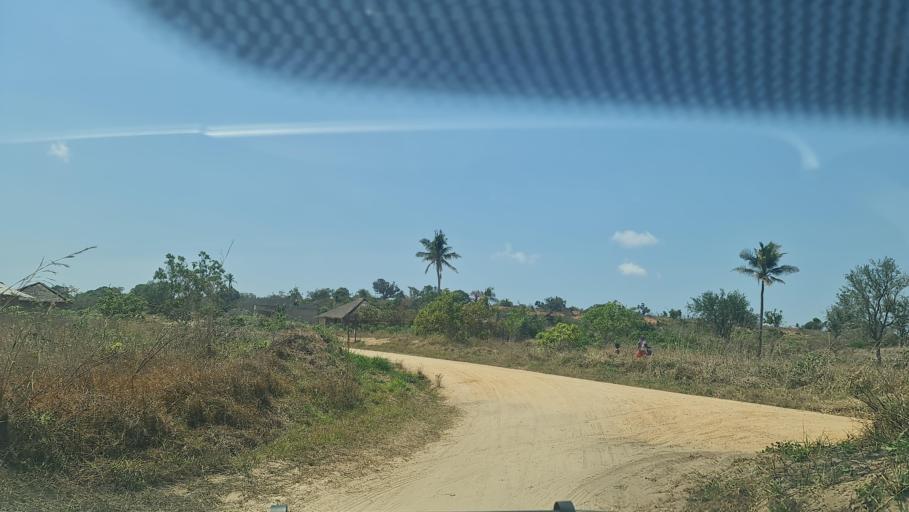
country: MZ
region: Nampula
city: Ilha de Mocambique
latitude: -15.2055
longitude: 40.5745
